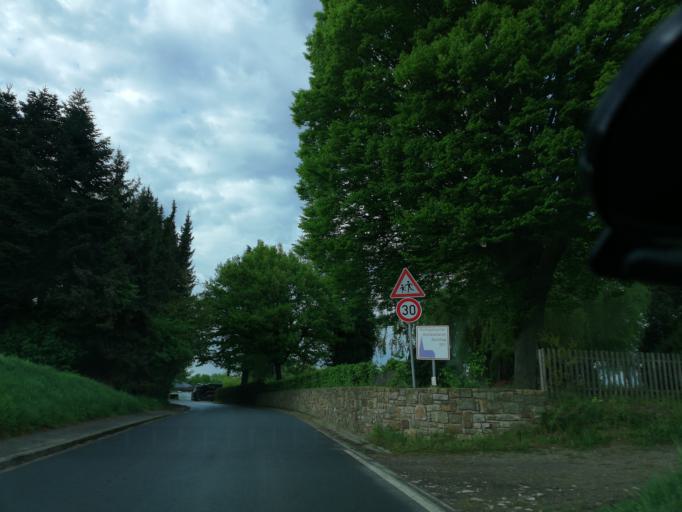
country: DE
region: Lower Saxony
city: Rinteln
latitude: 52.1337
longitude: 9.0677
